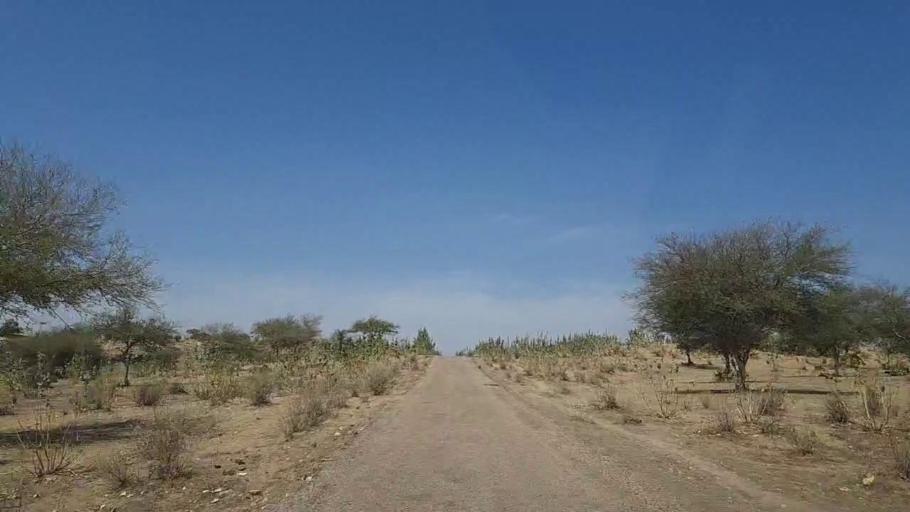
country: PK
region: Sindh
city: Mithi
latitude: 24.8569
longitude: 69.6698
